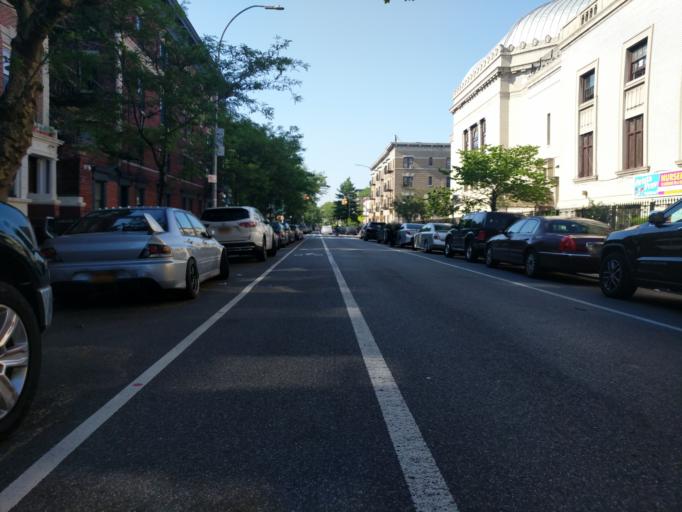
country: US
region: New York
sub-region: Kings County
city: Brooklyn
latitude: 40.6723
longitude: -73.9420
